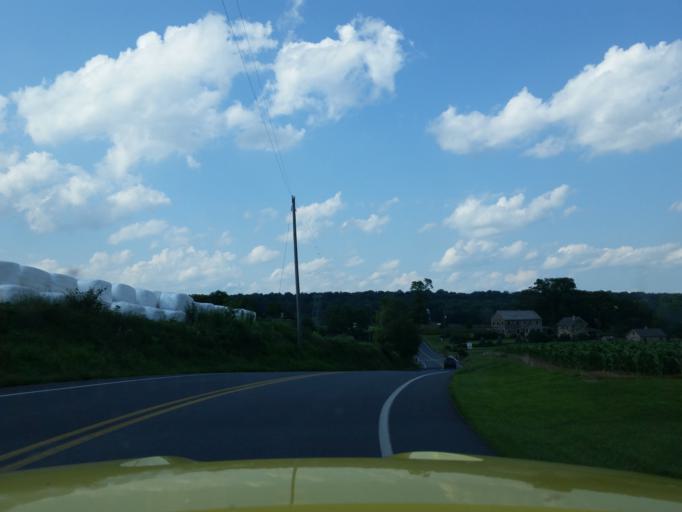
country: US
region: Pennsylvania
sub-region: Lebanon County
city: Campbelltown
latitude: 40.2122
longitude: -76.5067
